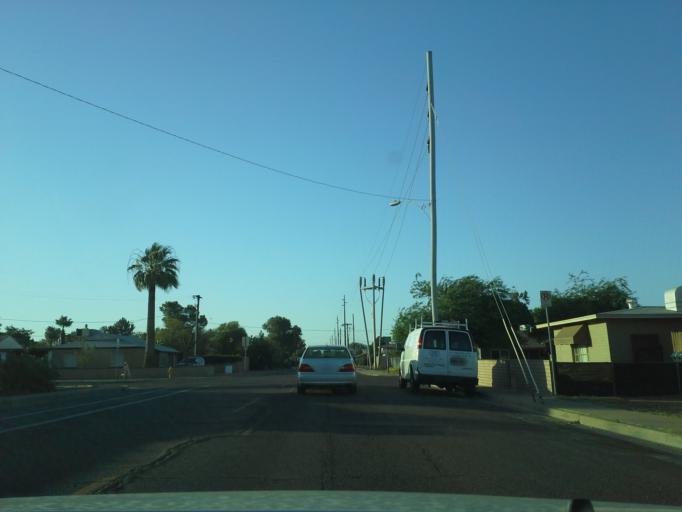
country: US
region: Arizona
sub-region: Maricopa County
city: Phoenix
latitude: 33.4979
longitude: -112.0781
